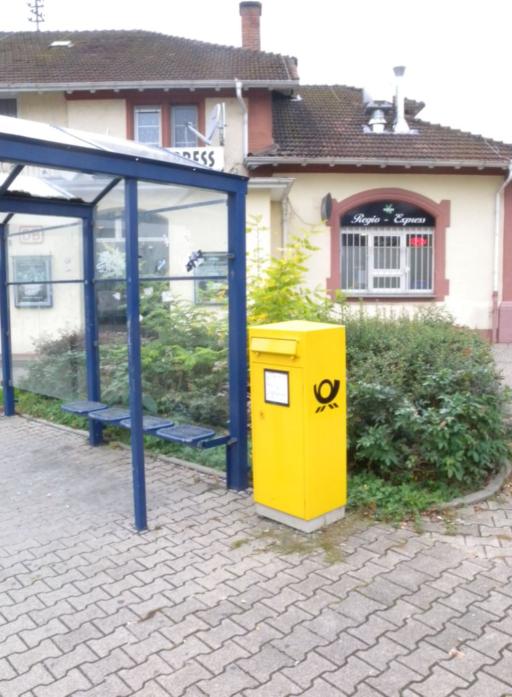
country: DE
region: Baden-Wuerttemberg
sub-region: Karlsruhe Region
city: Kronau
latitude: 49.2197
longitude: 8.6473
